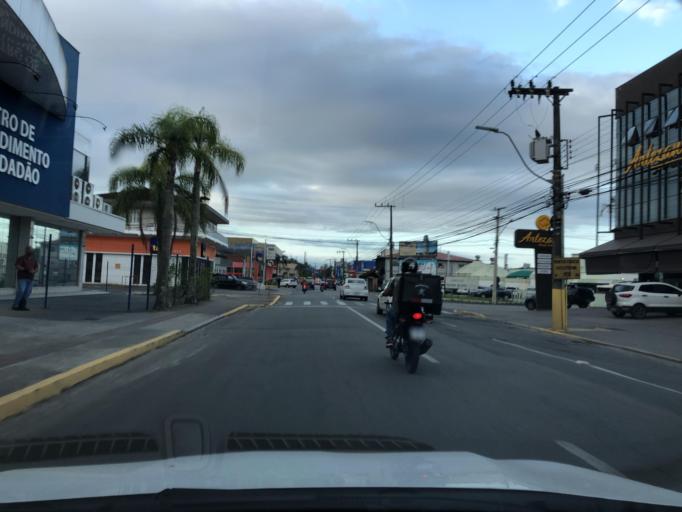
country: BR
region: Santa Catarina
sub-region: Joinville
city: Joinville
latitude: -26.2765
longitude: -48.8499
